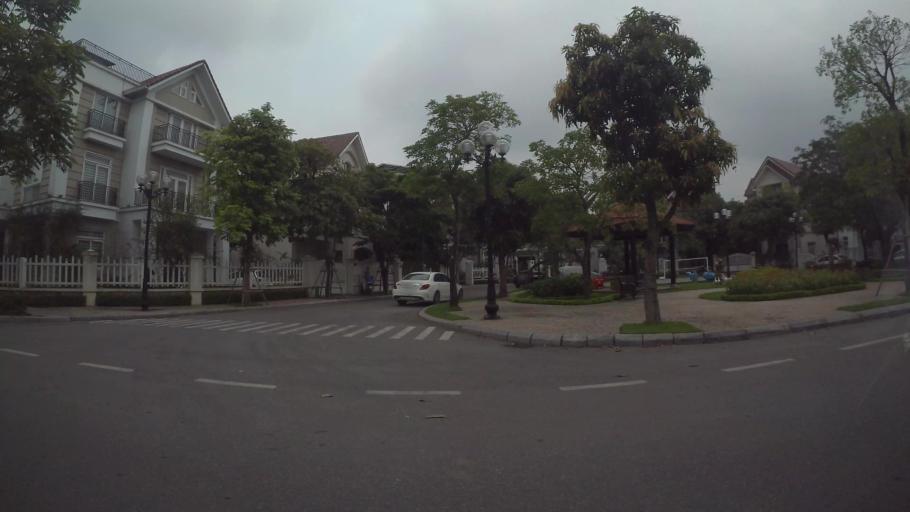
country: VN
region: Ha Noi
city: Trau Quy
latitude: 21.0408
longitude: 105.9184
